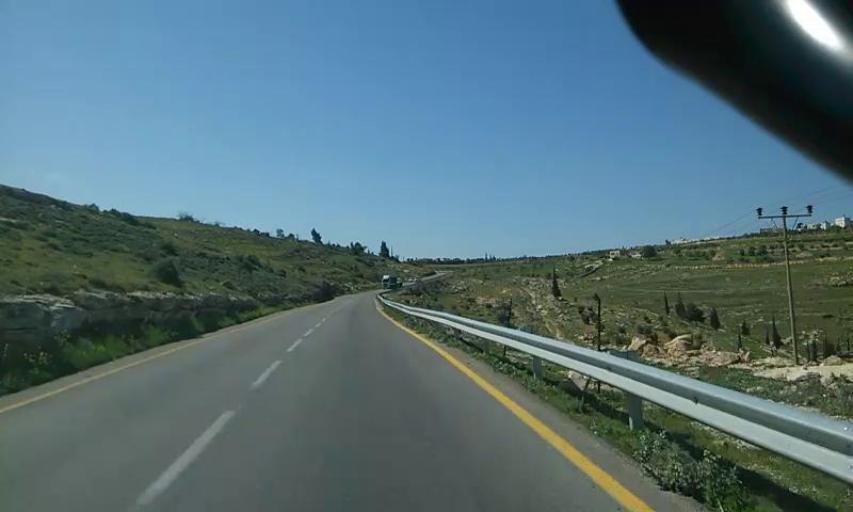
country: PS
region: West Bank
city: Jannatah
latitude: 31.6509
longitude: 35.2050
